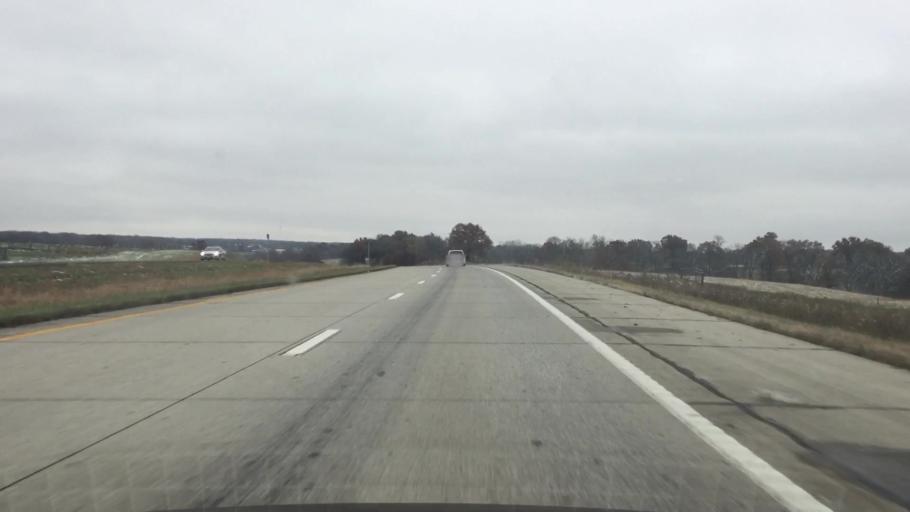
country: US
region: Missouri
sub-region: Saint Clair County
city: Osceola
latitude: 38.0260
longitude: -93.6738
